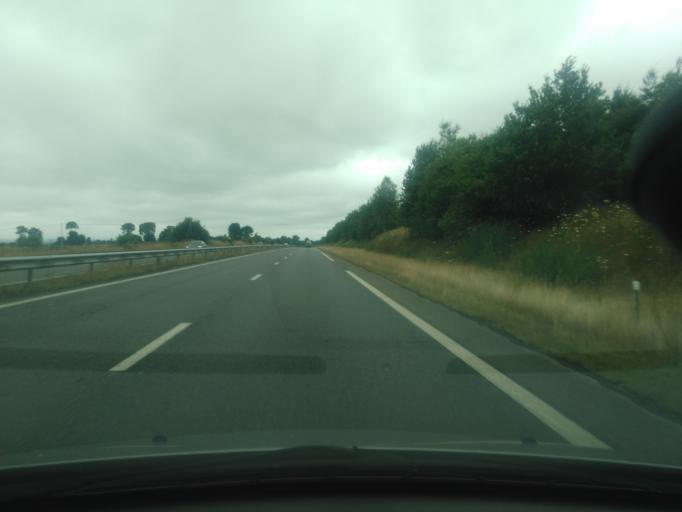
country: FR
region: Brittany
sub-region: Departement des Cotes-d'Armor
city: Jugon-les-Lacs
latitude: 48.4181
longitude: -2.2818
